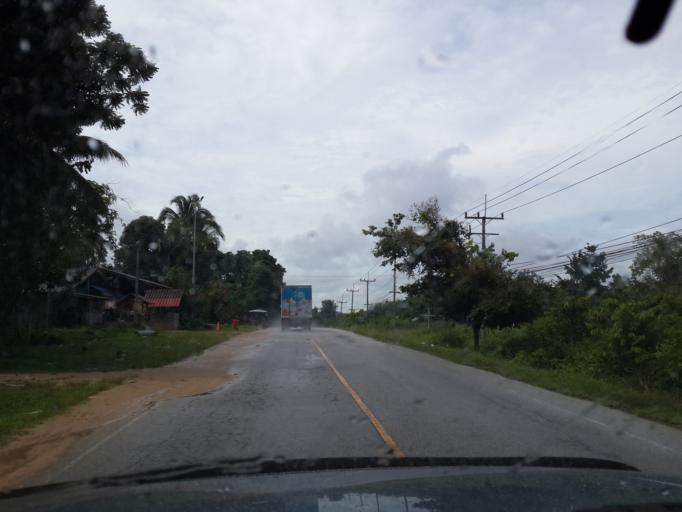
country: TH
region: Narathiwat
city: Rueso
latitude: 6.3753
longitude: 101.5284
